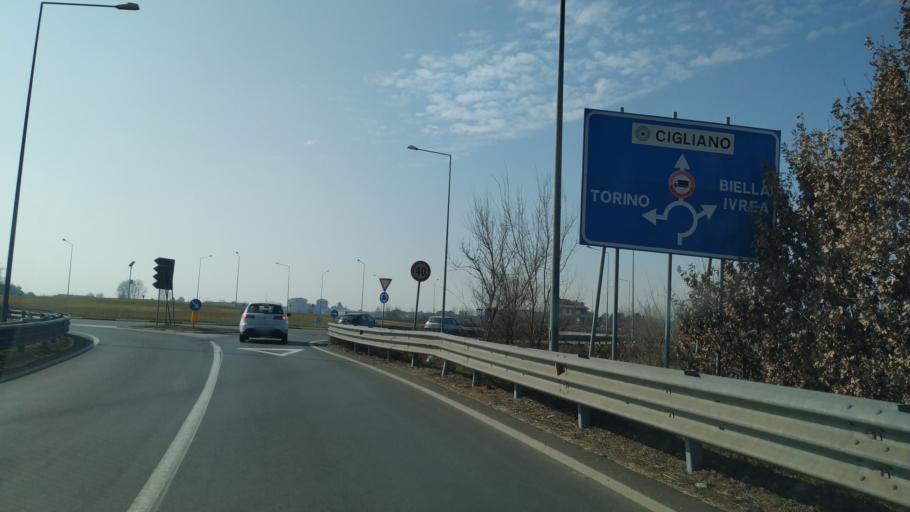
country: IT
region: Piedmont
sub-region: Provincia di Vercelli
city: Cigliano
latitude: 45.3137
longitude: 8.0422
